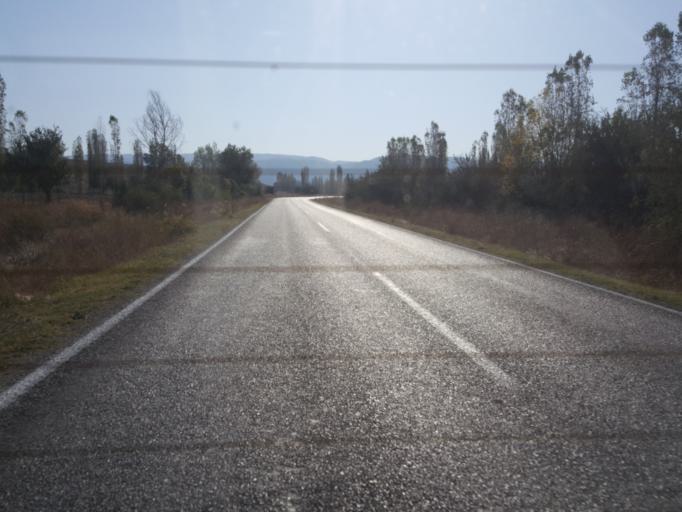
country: TR
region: Corum
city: Seydim
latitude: 40.5820
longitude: 34.6175
